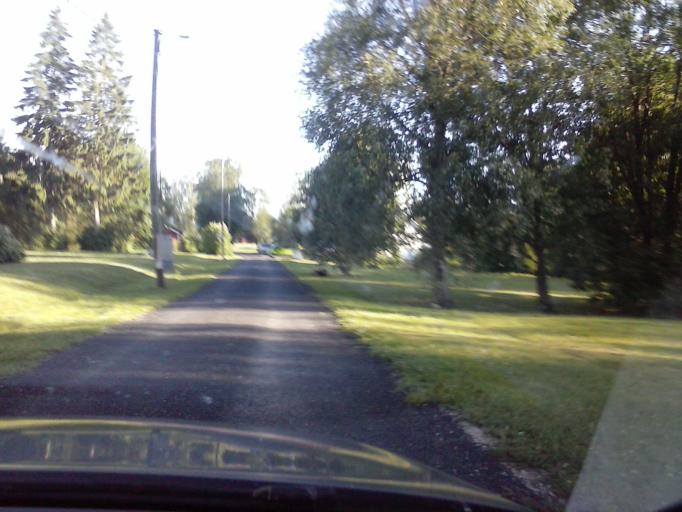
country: EE
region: Raplamaa
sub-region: Rapla vald
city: Rapla
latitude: 58.9990
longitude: 24.7853
